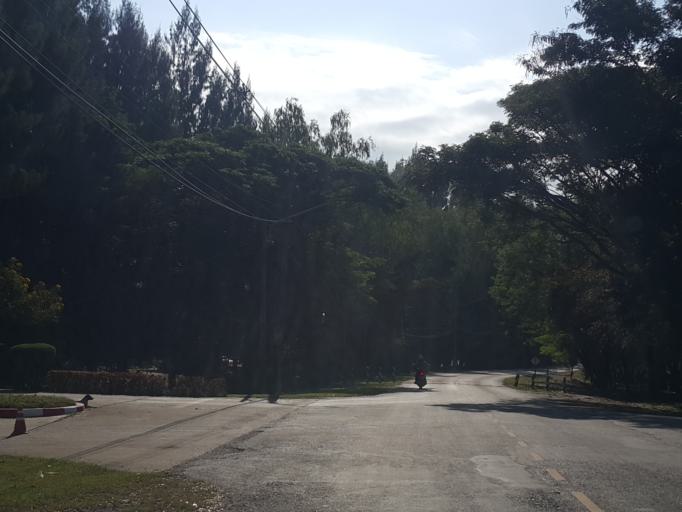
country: TH
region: Lampang
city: Mae Mo
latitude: 18.2934
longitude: 99.6716
